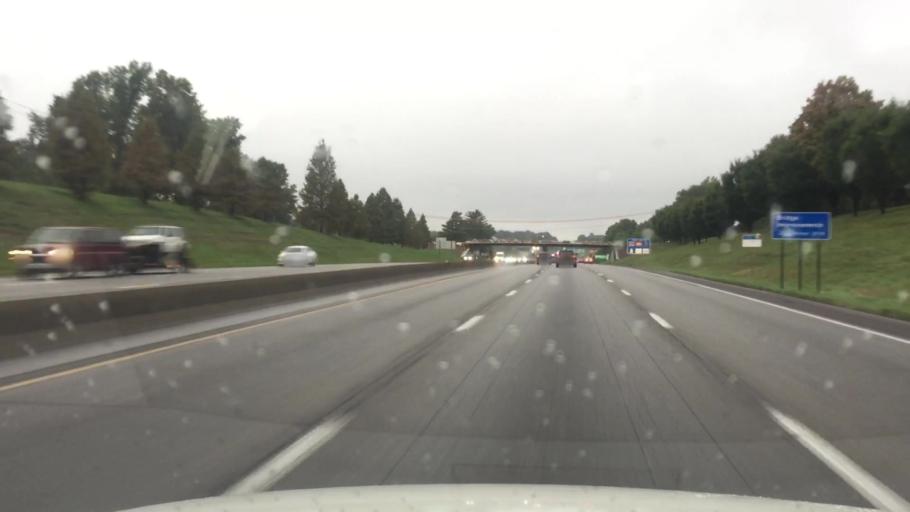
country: US
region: Missouri
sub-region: Jackson County
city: Independence
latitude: 39.0456
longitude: -94.4019
